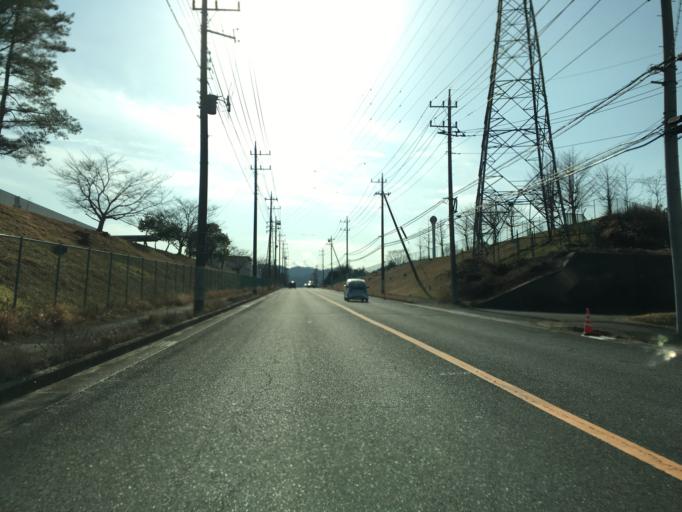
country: JP
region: Ibaraki
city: Takahagi
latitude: 36.7470
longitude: 140.6965
